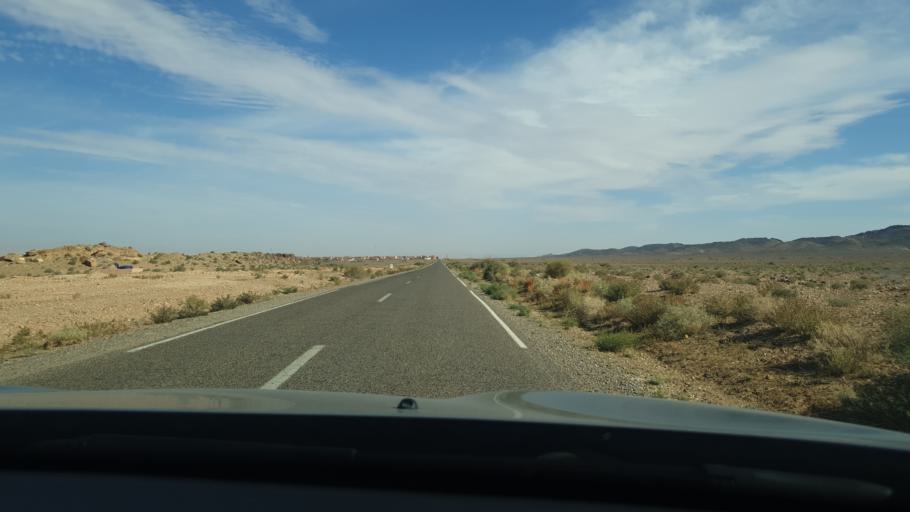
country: MA
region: Meknes-Tafilalet
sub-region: Errachidia
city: Goulmima
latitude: 31.5161
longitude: -4.9829
